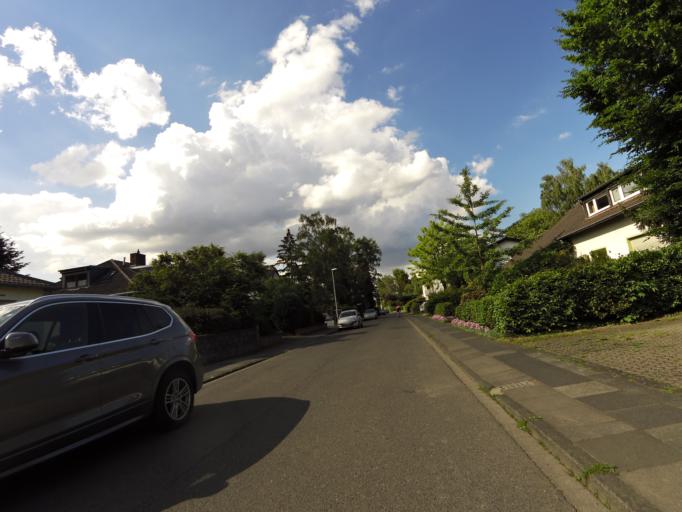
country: DE
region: North Rhine-Westphalia
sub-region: Regierungsbezirk Koln
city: Wachtberg
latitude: 50.6778
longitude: 7.0686
